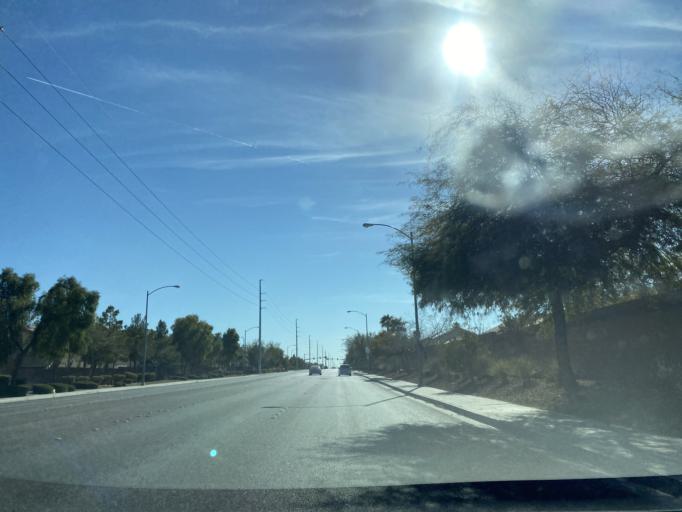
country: US
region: Nevada
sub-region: Clark County
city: North Las Vegas
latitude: 36.2351
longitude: -115.1436
